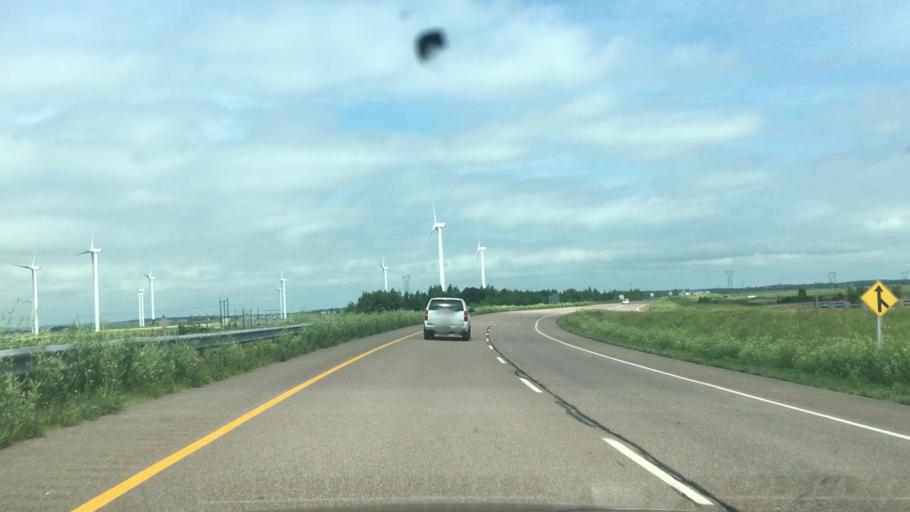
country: CA
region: Nova Scotia
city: Amherst
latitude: 45.8210
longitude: -64.2368
